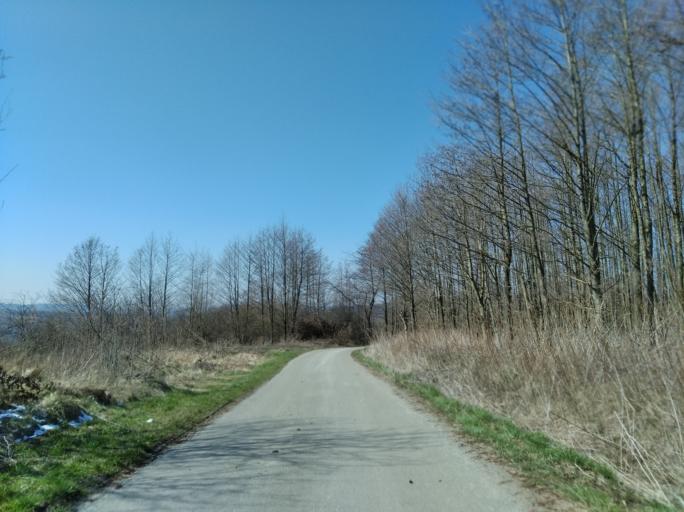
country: PL
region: Subcarpathian Voivodeship
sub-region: Powiat strzyzowski
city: Strzyzow
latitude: 49.8677
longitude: 21.8319
